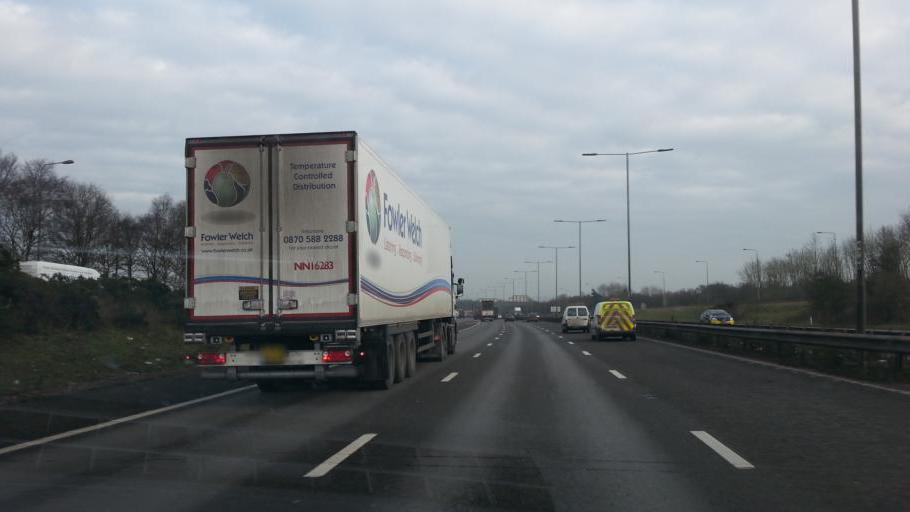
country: GB
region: England
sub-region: Solihull
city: Chelmsley Wood
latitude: 52.4766
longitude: -1.7038
